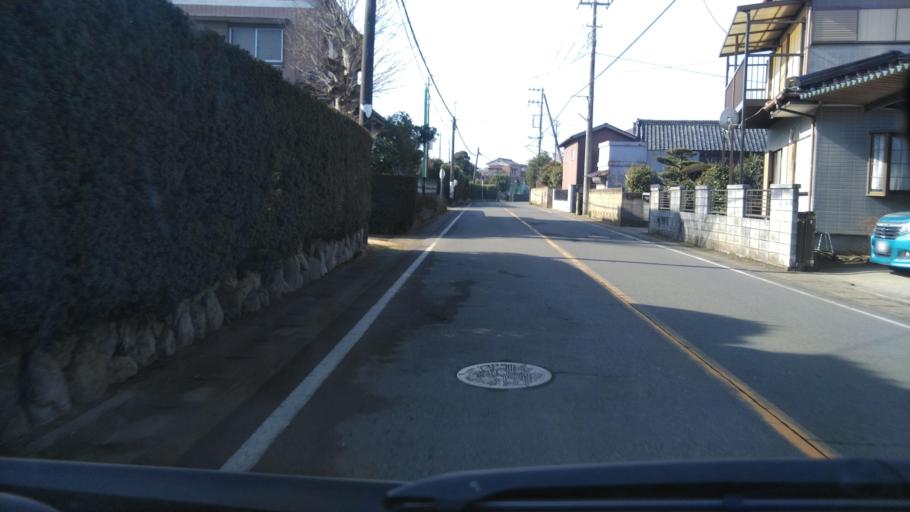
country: JP
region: Chiba
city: Katori-shi
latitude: 35.8937
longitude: 140.5162
